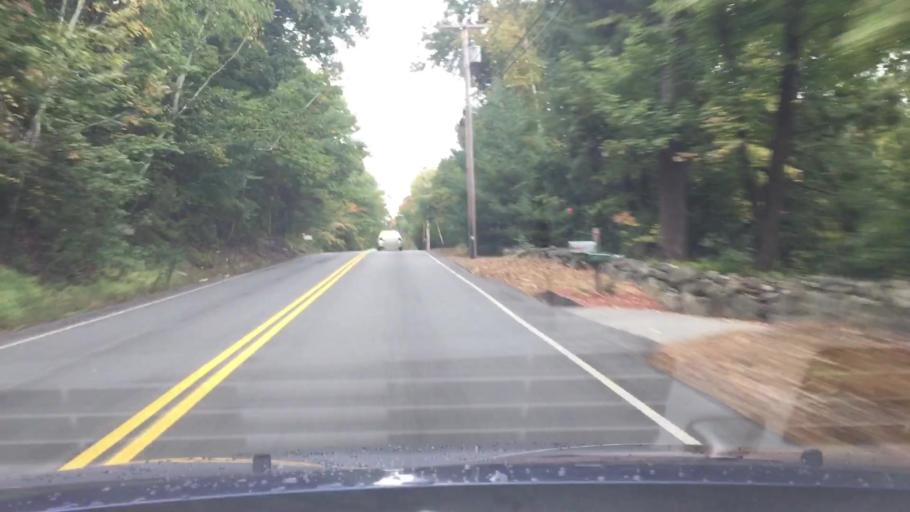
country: US
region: Massachusetts
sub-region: Middlesex County
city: Tyngsboro
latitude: 42.6899
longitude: -71.3795
